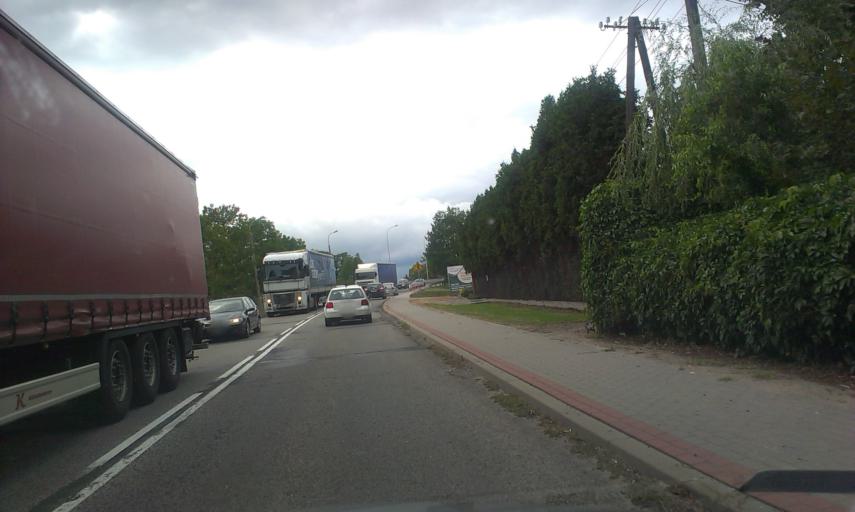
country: PL
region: Masovian Voivodeship
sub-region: Powiat zyrardowski
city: Mszczonow
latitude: 51.9759
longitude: 20.5079
